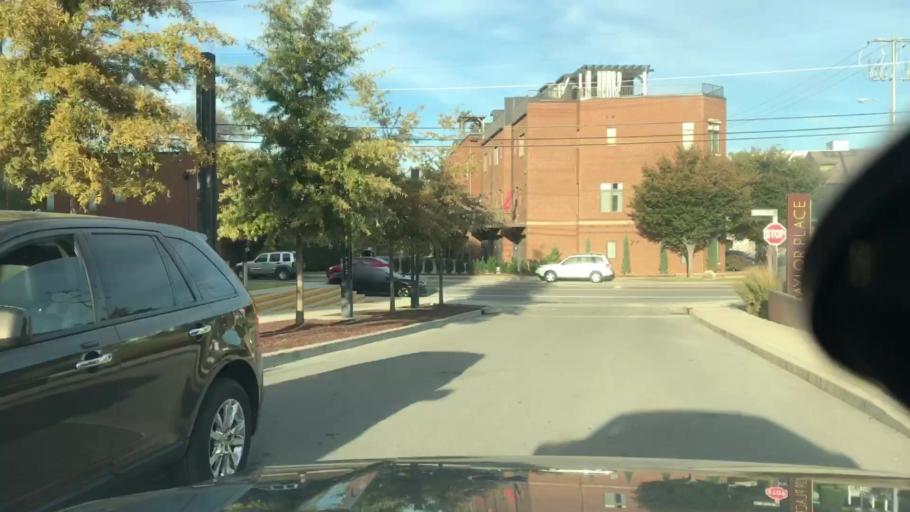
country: US
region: Tennessee
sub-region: Davidson County
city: Nashville
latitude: 36.1789
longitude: -86.7910
